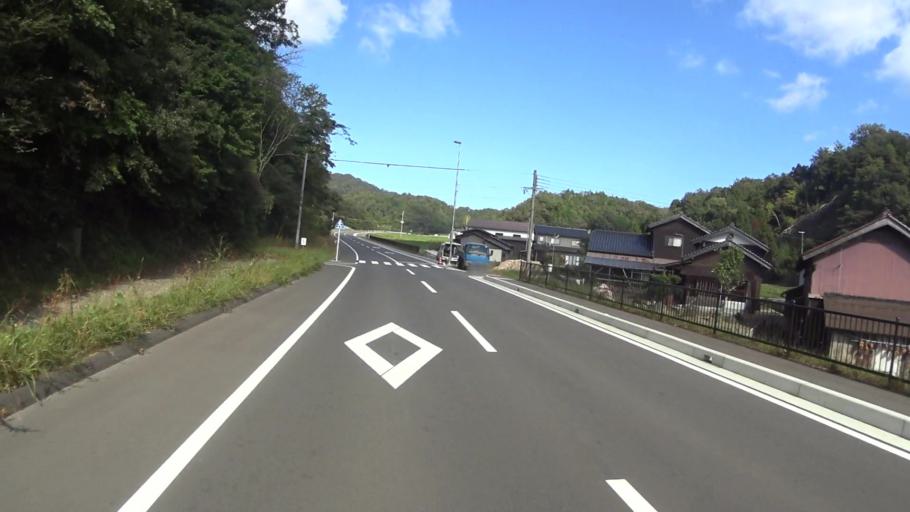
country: JP
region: Kyoto
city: Miyazu
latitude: 35.6104
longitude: 135.1343
